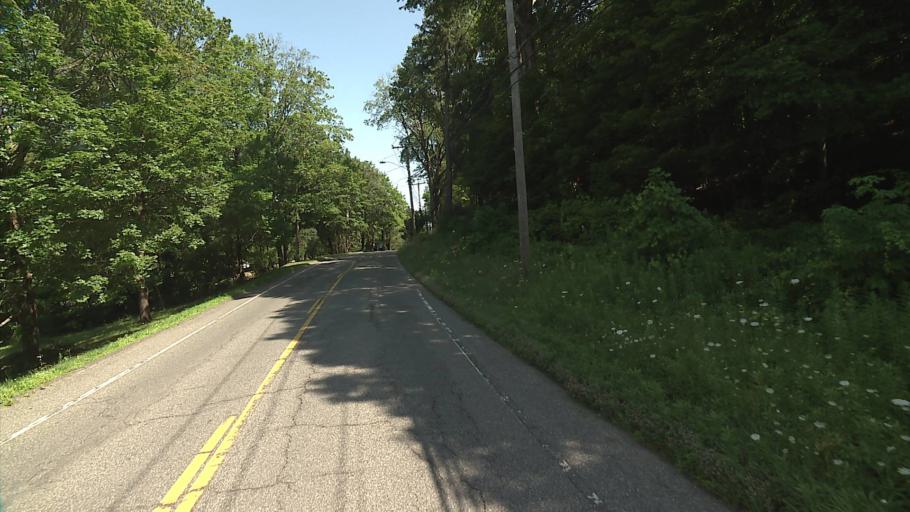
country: US
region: Connecticut
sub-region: Litchfield County
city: Winchester Center
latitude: 41.9820
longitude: -73.2007
